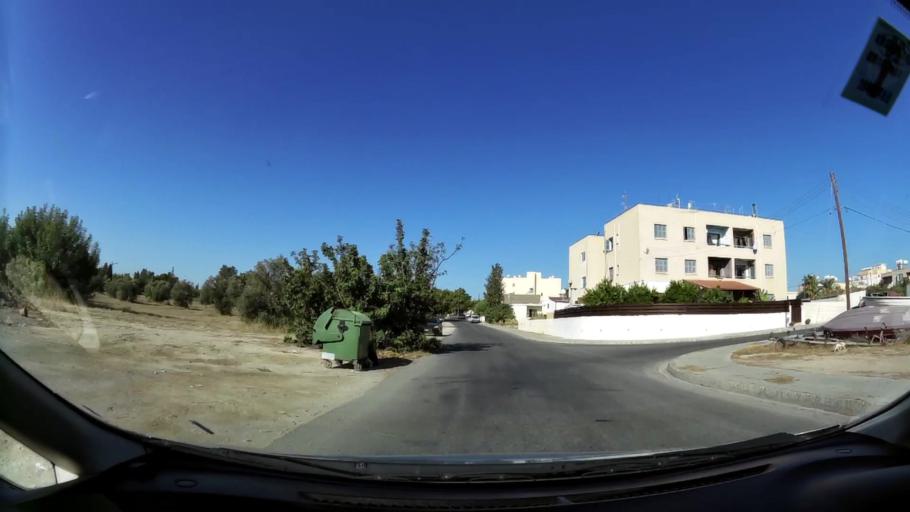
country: CY
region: Larnaka
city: Larnaca
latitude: 34.9266
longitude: 33.6105
